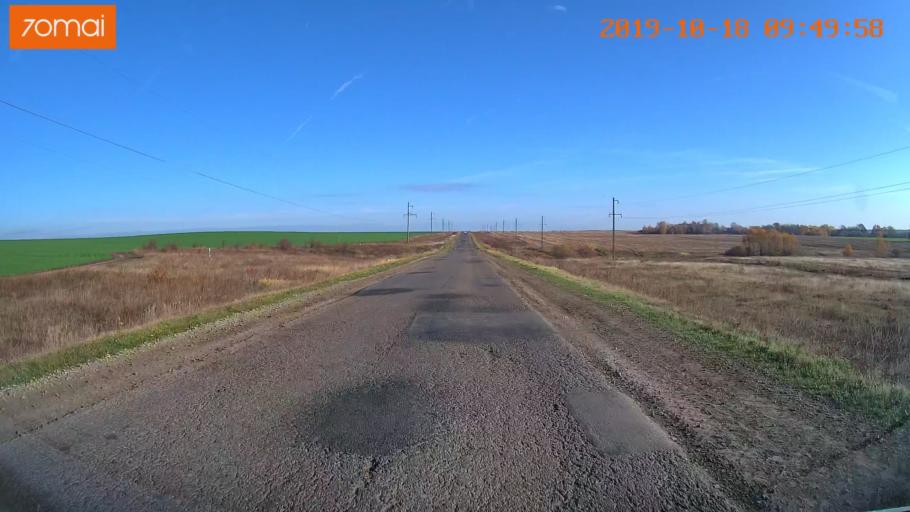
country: RU
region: Tula
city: Kazachka
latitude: 53.3238
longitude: 38.2710
